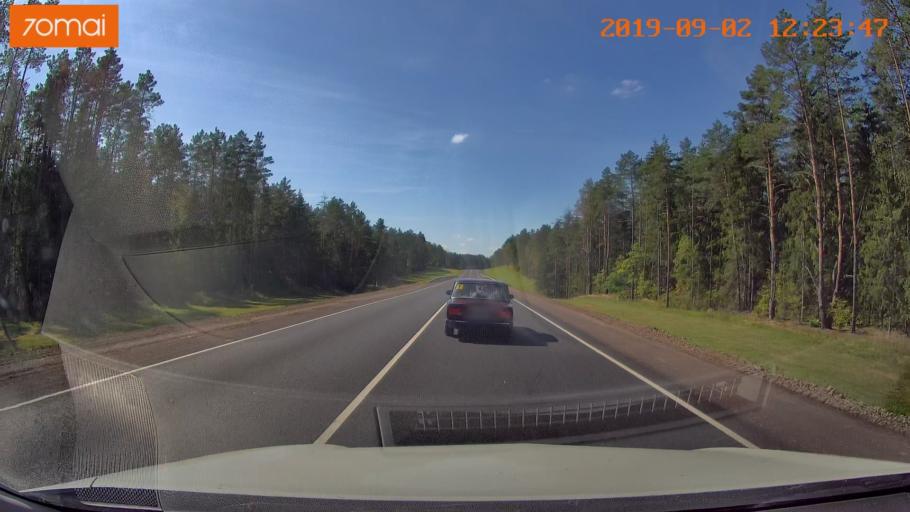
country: RU
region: Smolensk
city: Shumyachi
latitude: 53.8731
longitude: 32.6176
